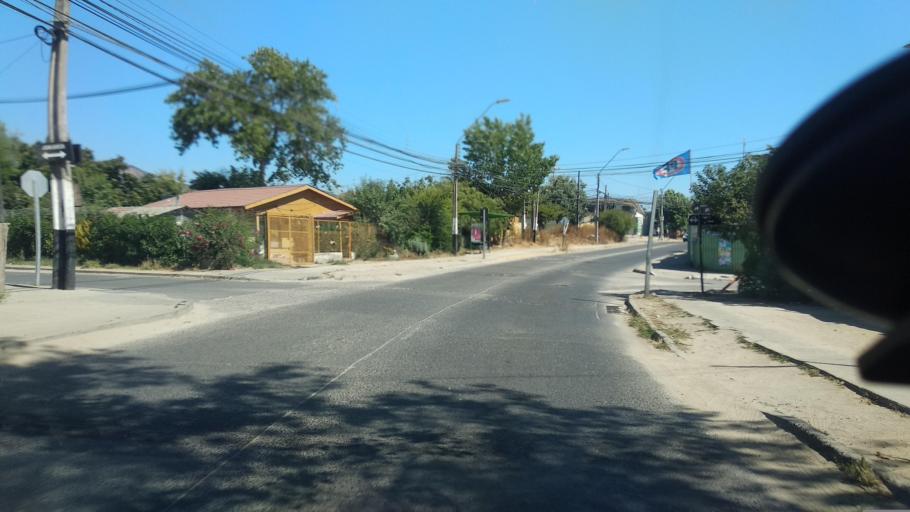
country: CL
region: Valparaiso
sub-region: Provincia de Marga Marga
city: Villa Alemana
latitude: -33.0578
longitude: -71.3725
